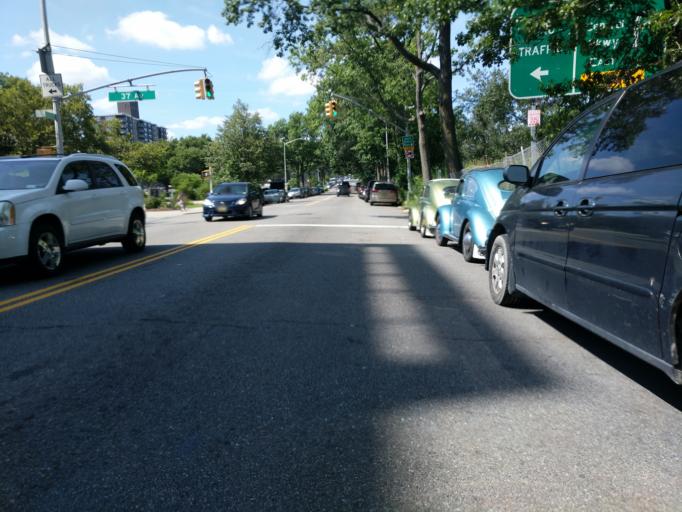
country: US
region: New York
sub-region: Queens County
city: Borough of Queens
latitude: 40.7547
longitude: -73.8537
